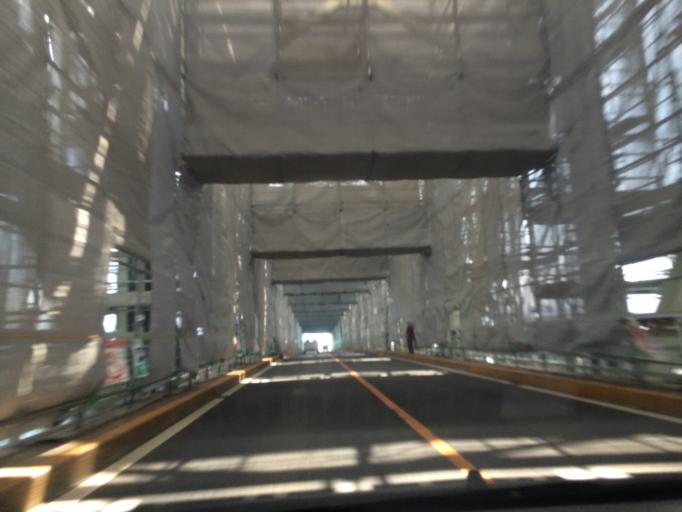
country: JP
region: Shimane
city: Sakaiminato
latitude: 35.5495
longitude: 133.2444
